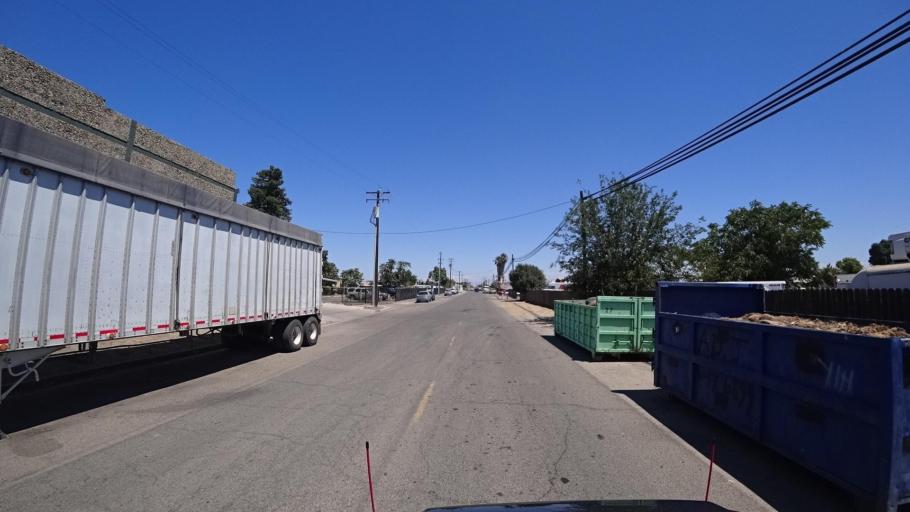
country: US
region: California
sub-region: Fresno County
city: Easton
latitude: 36.6831
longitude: -119.7457
